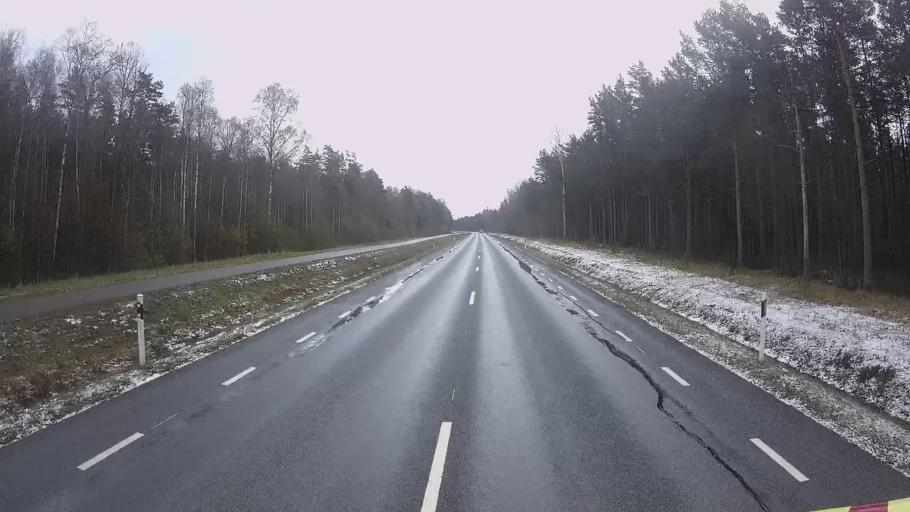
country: EE
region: Hiiumaa
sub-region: Kaerdla linn
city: Kardla
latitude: 59.0003
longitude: 22.7004
